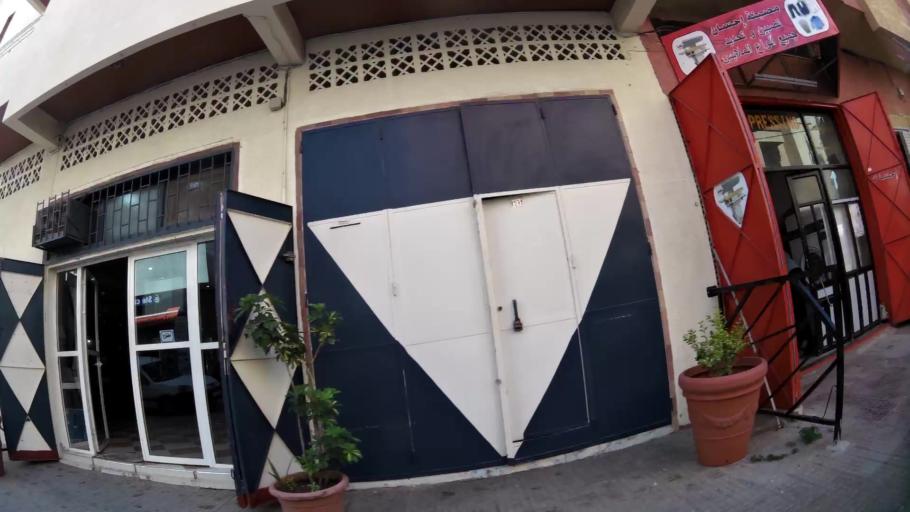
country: MA
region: Rabat-Sale-Zemmour-Zaer
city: Sale
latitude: 34.0411
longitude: -6.7833
